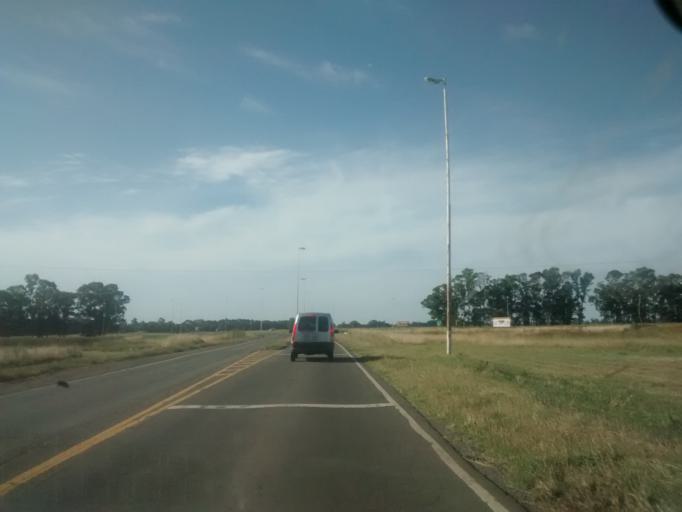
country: AR
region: Buenos Aires
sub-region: Partido de Ayacucho
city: Ayacucho
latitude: -37.2290
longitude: -58.4950
